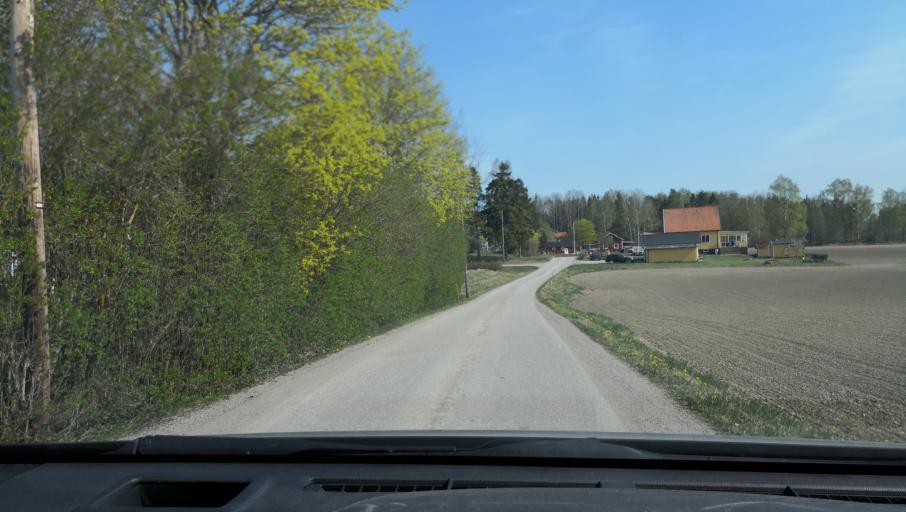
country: SE
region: Vaestmanland
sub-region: Sala Kommun
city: Sala
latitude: 60.0074
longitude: 16.7061
